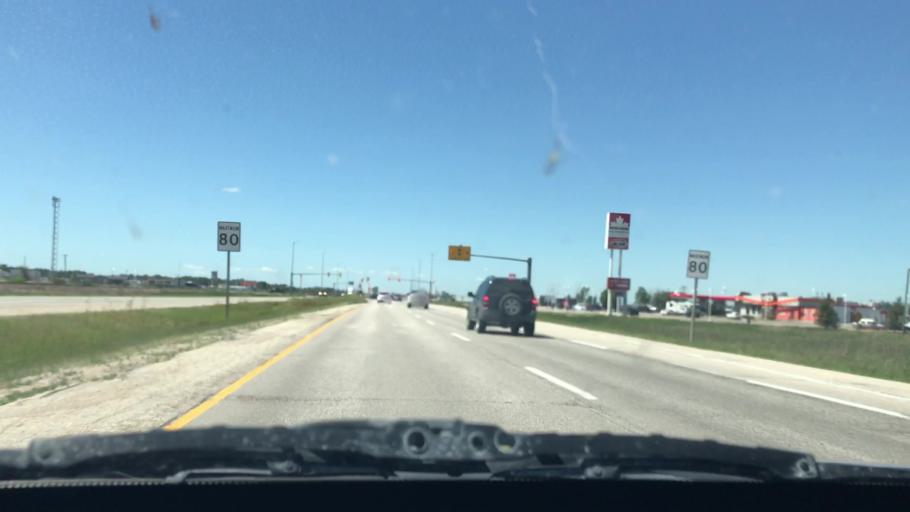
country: CA
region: Manitoba
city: Winnipeg
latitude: 49.8189
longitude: -96.9325
